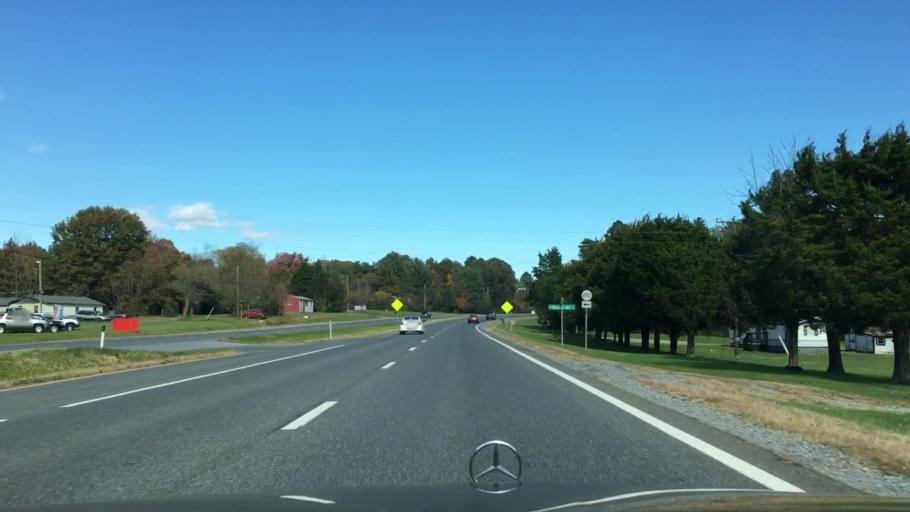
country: US
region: Virginia
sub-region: Campbell County
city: Rustburg
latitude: 37.2082
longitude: -79.2018
